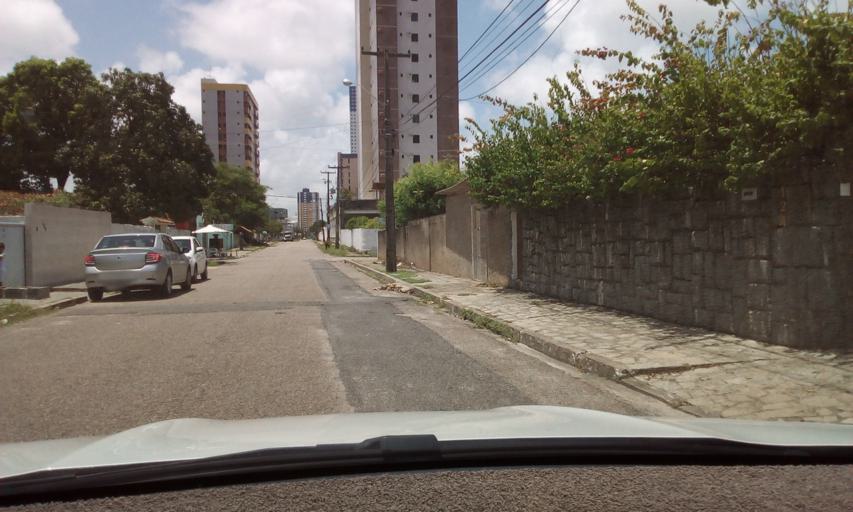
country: BR
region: Paraiba
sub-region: Joao Pessoa
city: Joao Pessoa
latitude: -7.1077
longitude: -34.8390
